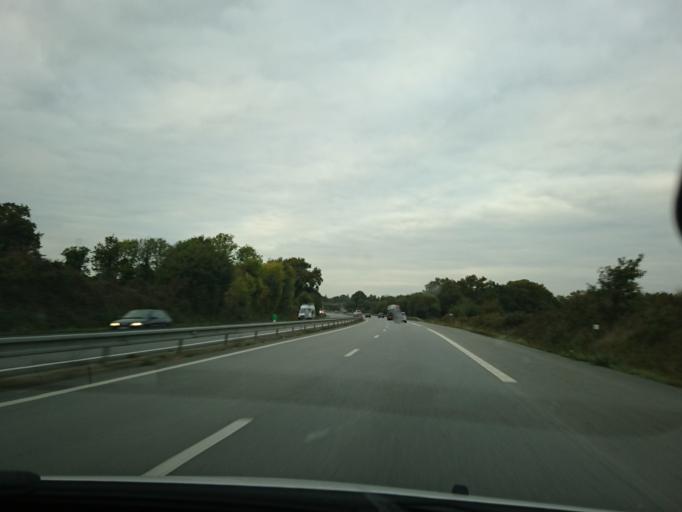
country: FR
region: Brittany
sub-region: Departement du Morbihan
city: Auray
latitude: 47.6764
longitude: -3.0173
